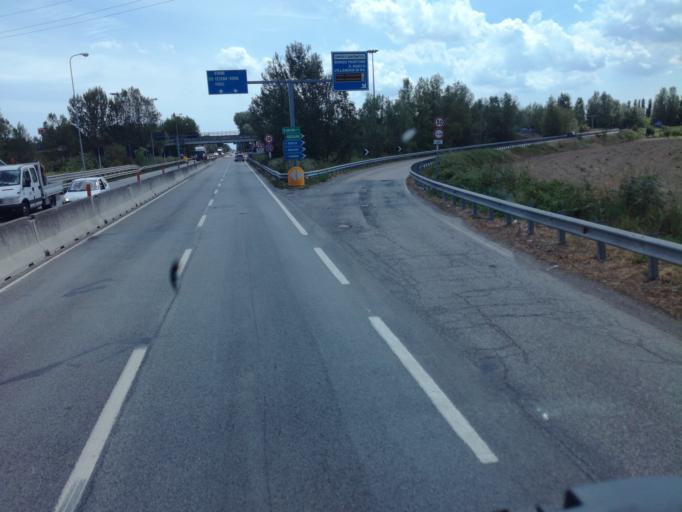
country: IT
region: Emilia-Romagna
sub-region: Provincia di Ravenna
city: Ravenna
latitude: 44.4125
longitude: 12.1712
